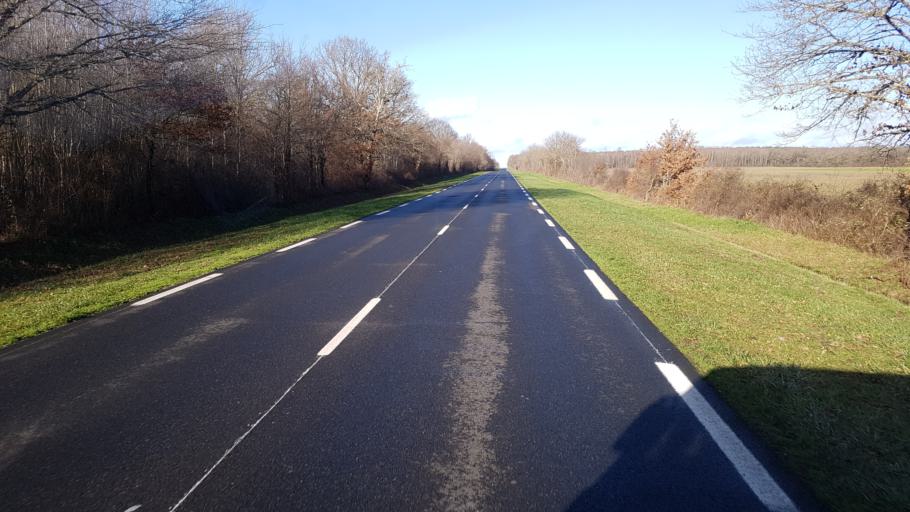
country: FR
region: Centre
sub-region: Departement du Loir-et-Cher
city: Nouan-le-Fuzelier
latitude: 47.4895
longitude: 2.0387
